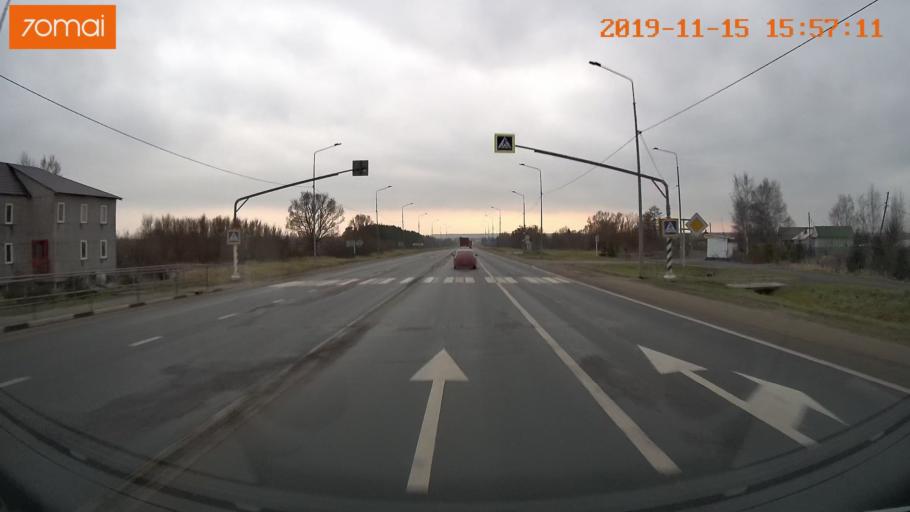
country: RU
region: Jaroslavl
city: Yaroslavl
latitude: 57.8331
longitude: 39.9659
